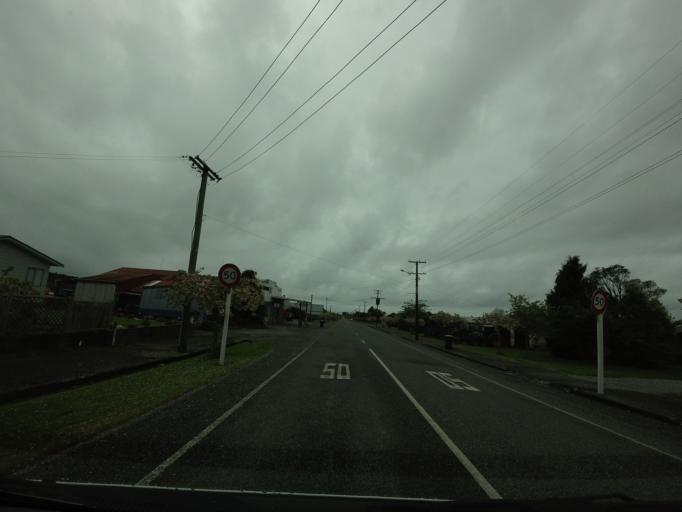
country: NZ
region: West Coast
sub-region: Westland District
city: Hokitika
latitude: -42.8974
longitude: 170.8156
